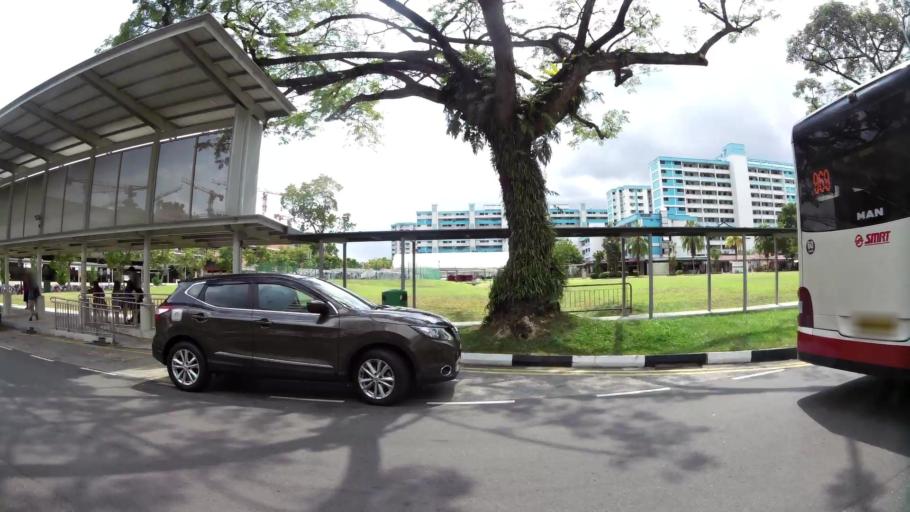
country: MY
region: Johor
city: Kampung Pasir Gudang Baru
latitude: 1.4304
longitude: 103.8344
